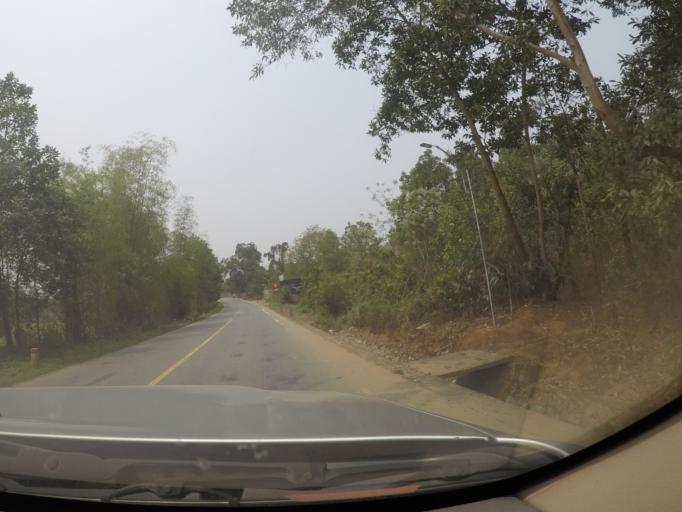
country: VN
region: Thanh Hoa
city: Thi Tran Ngoc Lac
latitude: 20.1419
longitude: 105.4281
